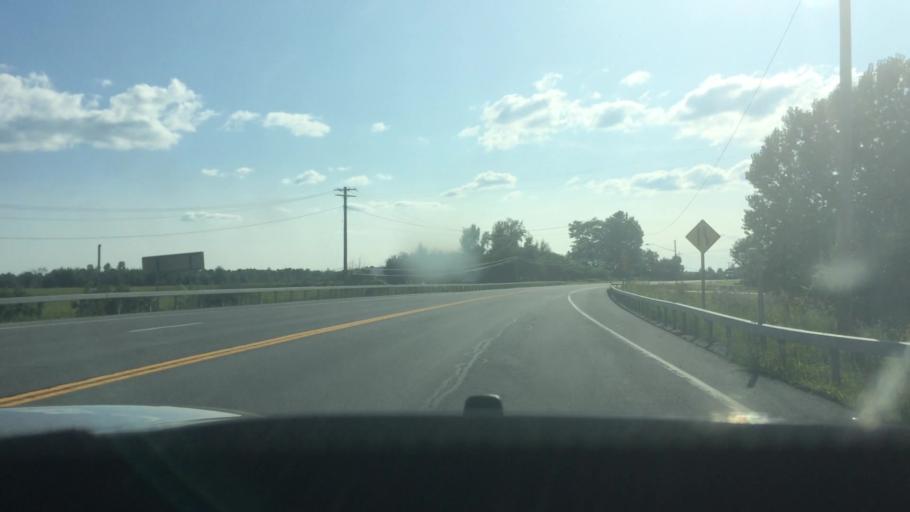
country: US
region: New York
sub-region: St. Lawrence County
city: Hannawa Falls
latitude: 44.6940
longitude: -74.6645
